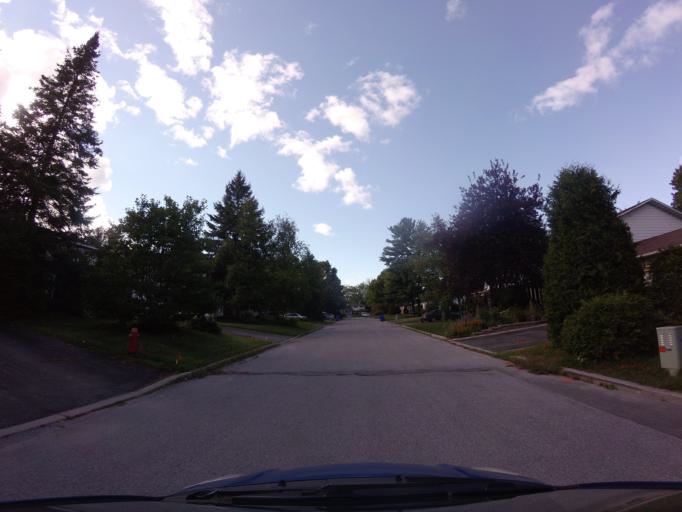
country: CA
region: Quebec
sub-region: Outaouais
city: Gatineau
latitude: 45.4887
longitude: -75.7325
